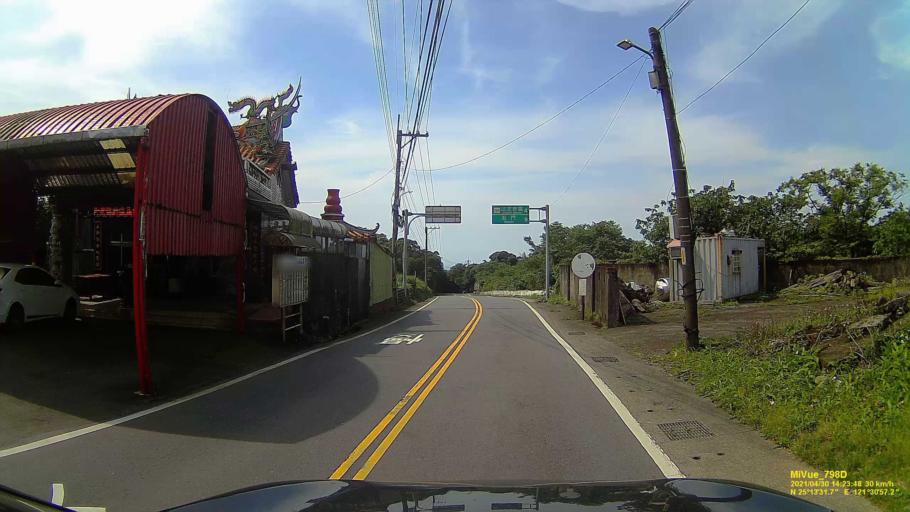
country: TW
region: Taipei
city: Taipei
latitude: 25.2257
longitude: 121.5158
